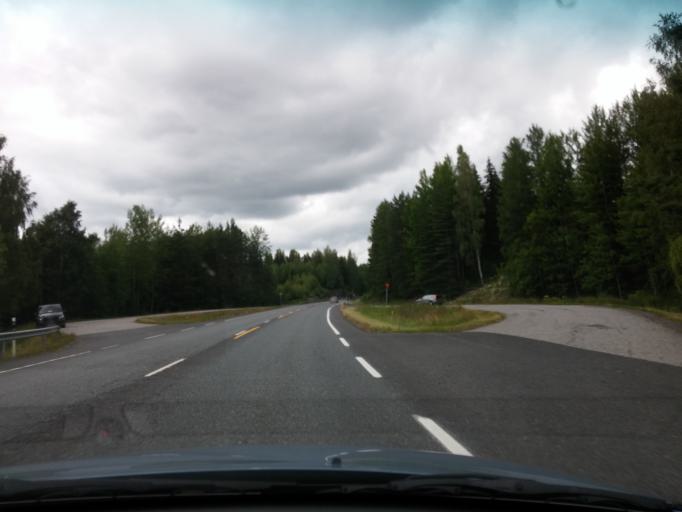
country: FI
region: Uusimaa
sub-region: Porvoo
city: Porvoo
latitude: 60.4303
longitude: 25.5760
